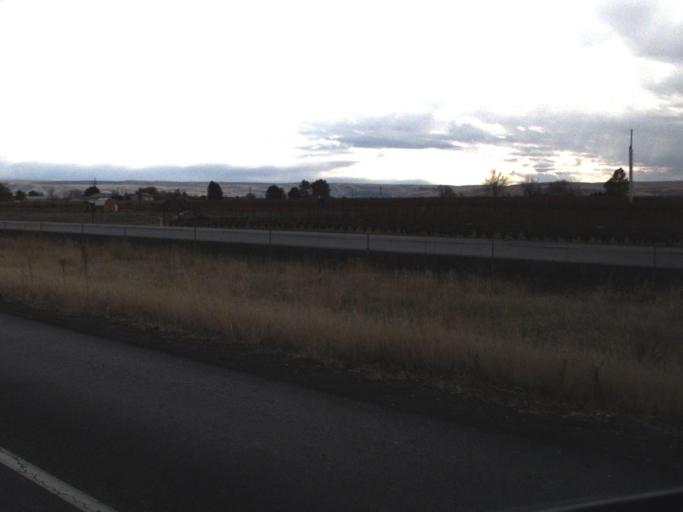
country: US
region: Washington
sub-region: Walla Walla County
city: Burbank
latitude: 46.1779
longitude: -118.9681
